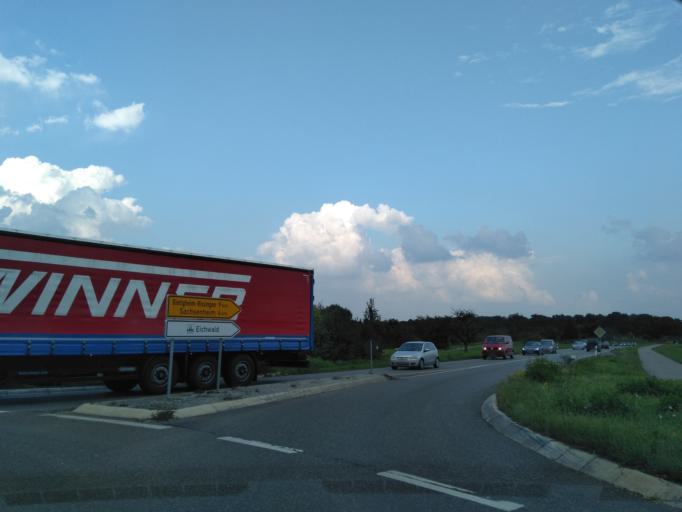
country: DE
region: Baden-Wuerttemberg
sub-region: Regierungsbezirk Stuttgart
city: Sersheim
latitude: 48.9501
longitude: 9.0179
